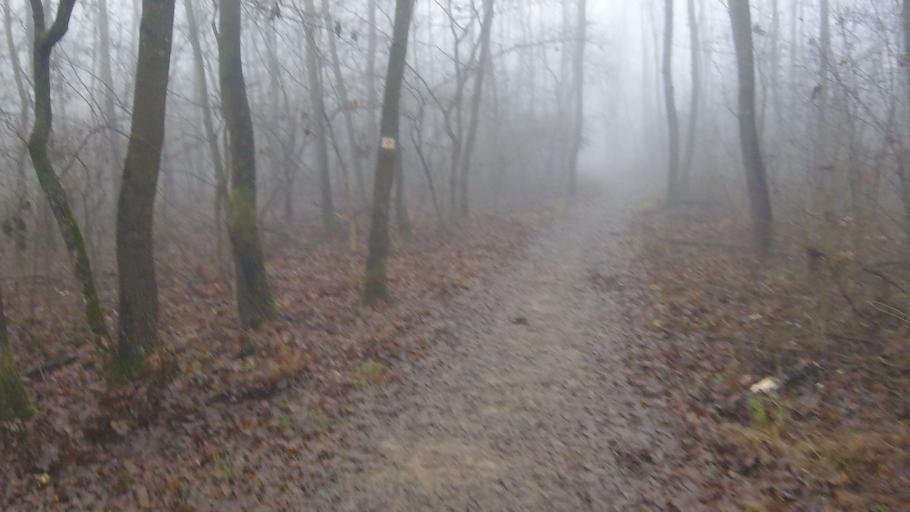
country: HU
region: Pest
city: Budakeszi
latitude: 47.5272
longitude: 18.9332
